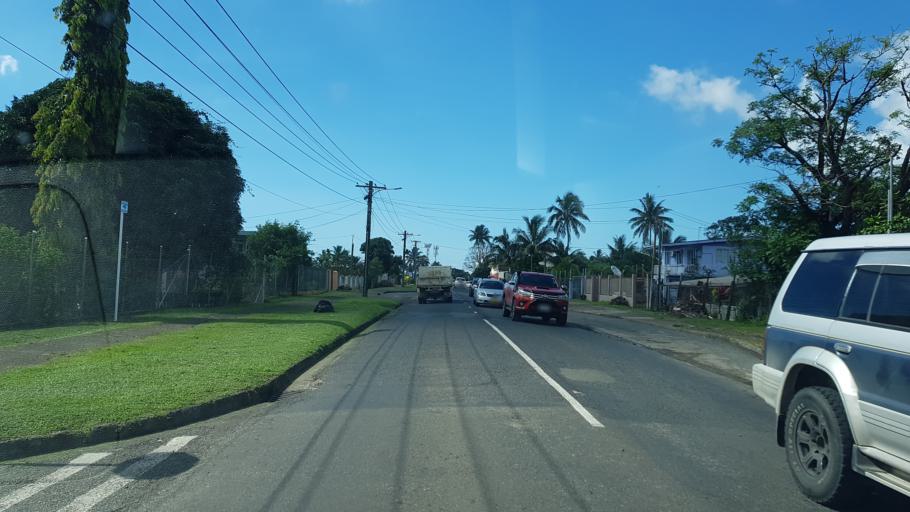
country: FJ
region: Central
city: Suva
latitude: -18.1333
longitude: 178.4591
